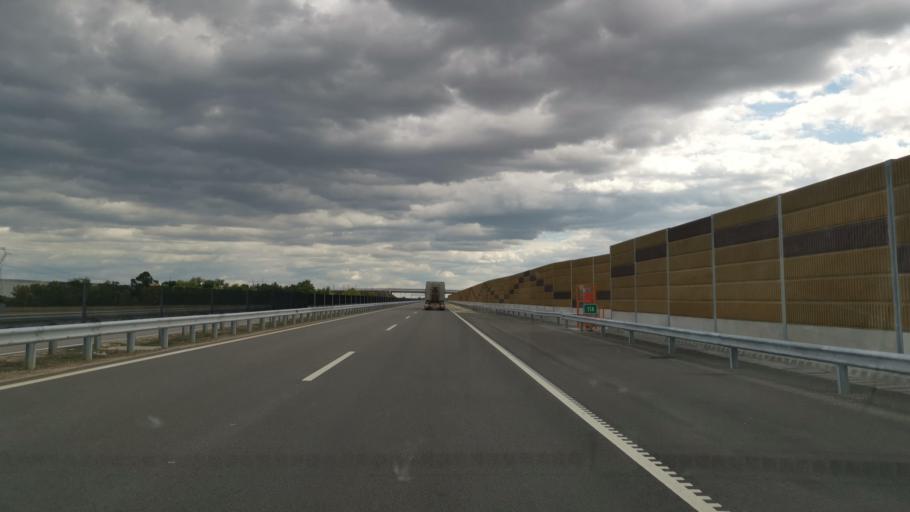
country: HU
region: Jasz-Nagykun-Szolnok
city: Tiszapuspoki
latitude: 47.1980
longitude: 20.3303
